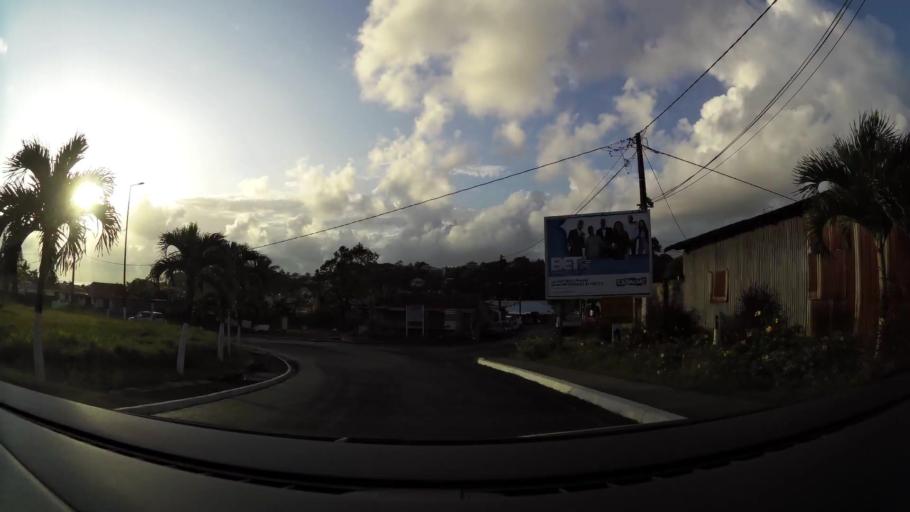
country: GP
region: Guadeloupe
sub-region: Guadeloupe
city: Petit-Bourg
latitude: 16.1927
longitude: -61.5953
